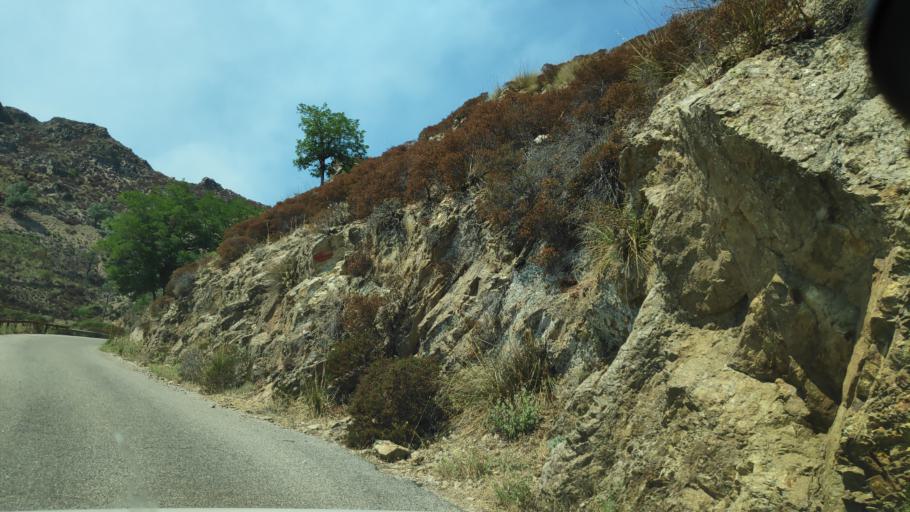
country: IT
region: Calabria
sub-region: Provincia di Reggio Calabria
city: Bova
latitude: 37.9999
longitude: 15.9279
